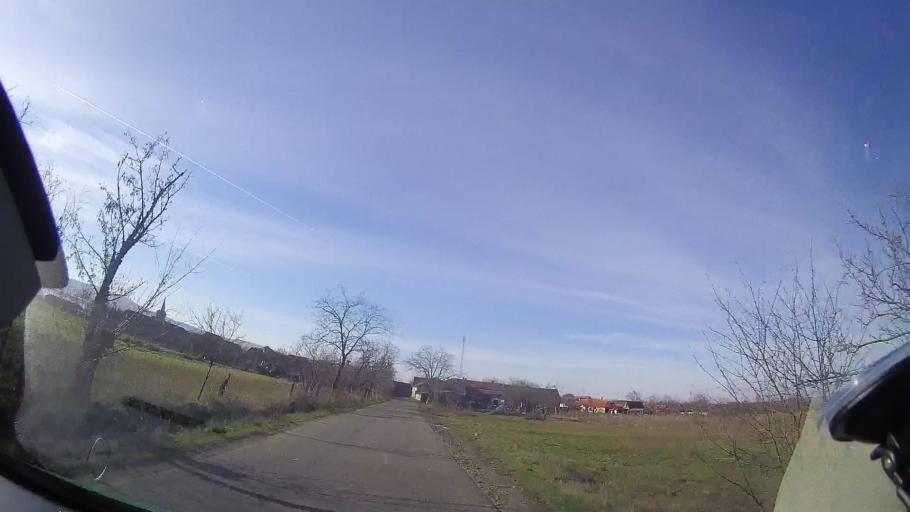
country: RO
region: Bihor
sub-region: Comuna Auseu
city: Grosi
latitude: 47.0274
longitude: 22.4764
